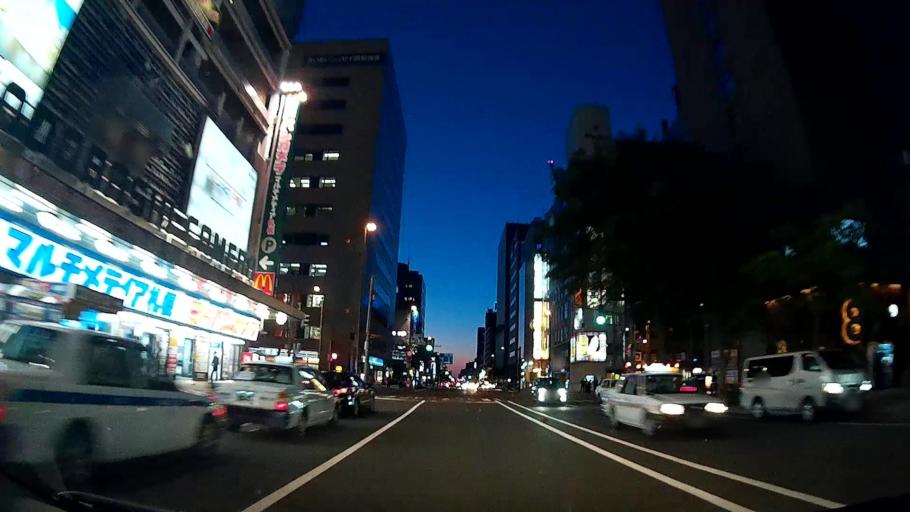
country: JP
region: Hokkaido
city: Sapporo
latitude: 43.0683
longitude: 141.3484
